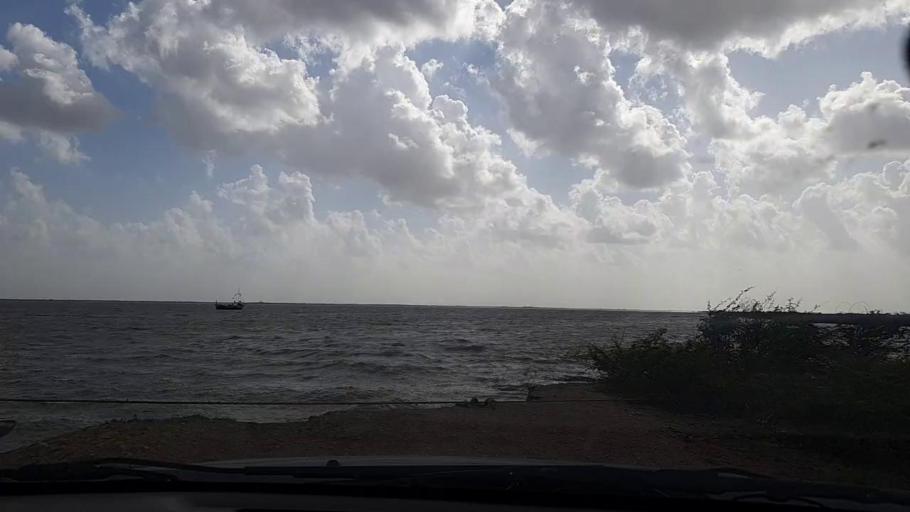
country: PK
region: Sindh
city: Keti Bandar
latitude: 24.0847
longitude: 67.6136
